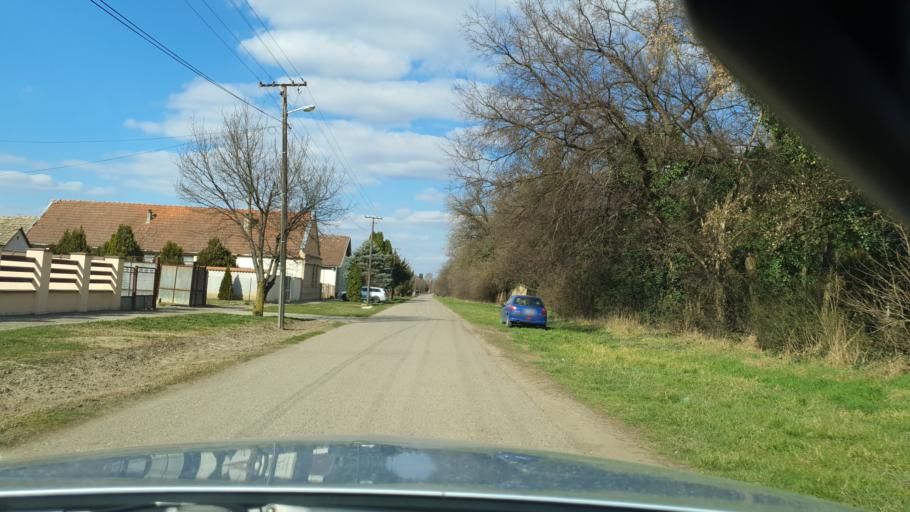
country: RS
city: Kulpin
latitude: 45.4011
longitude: 19.5858
